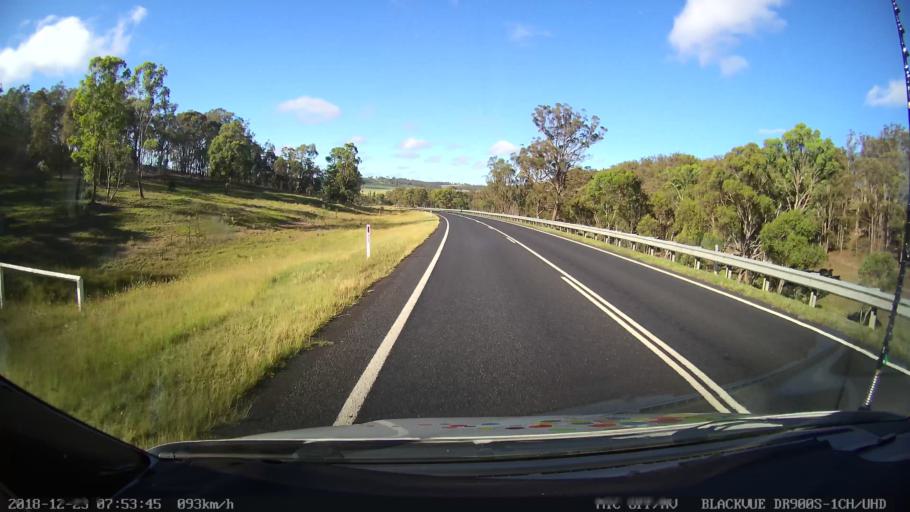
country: AU
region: New South Wales
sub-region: Armidale Dumaresq
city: Armidale
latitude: -30.5388
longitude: 151.8049
